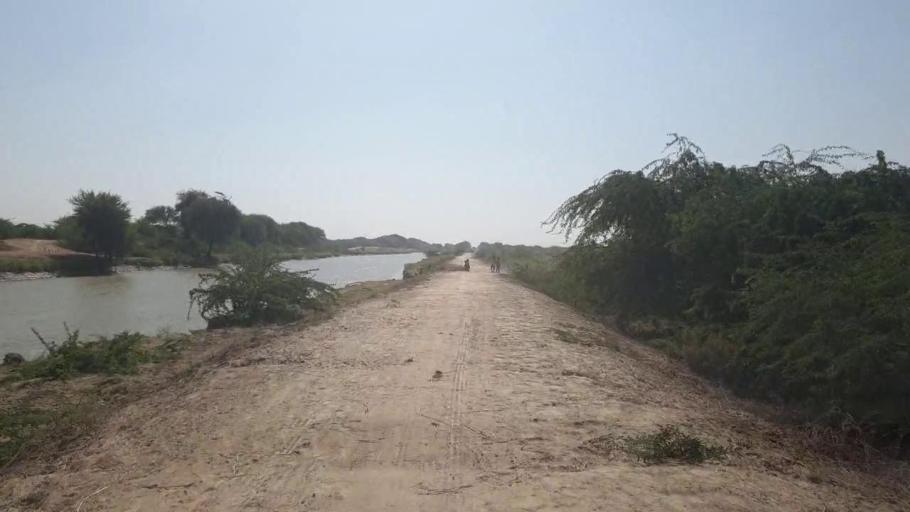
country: PK
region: Sindh
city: Talhar
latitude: 24.8192
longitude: 68.7935
